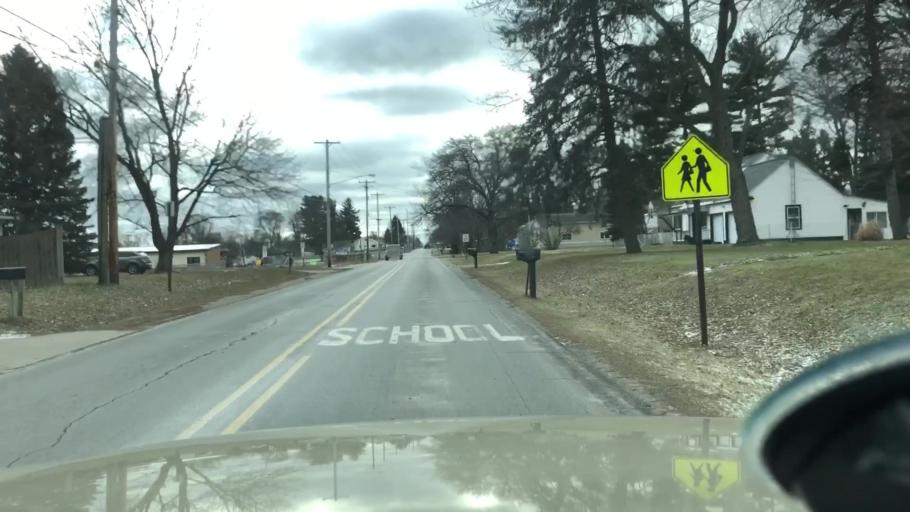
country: US
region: Michigan
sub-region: Jackson County
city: Jackson
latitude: 42.2616
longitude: -84.3649
